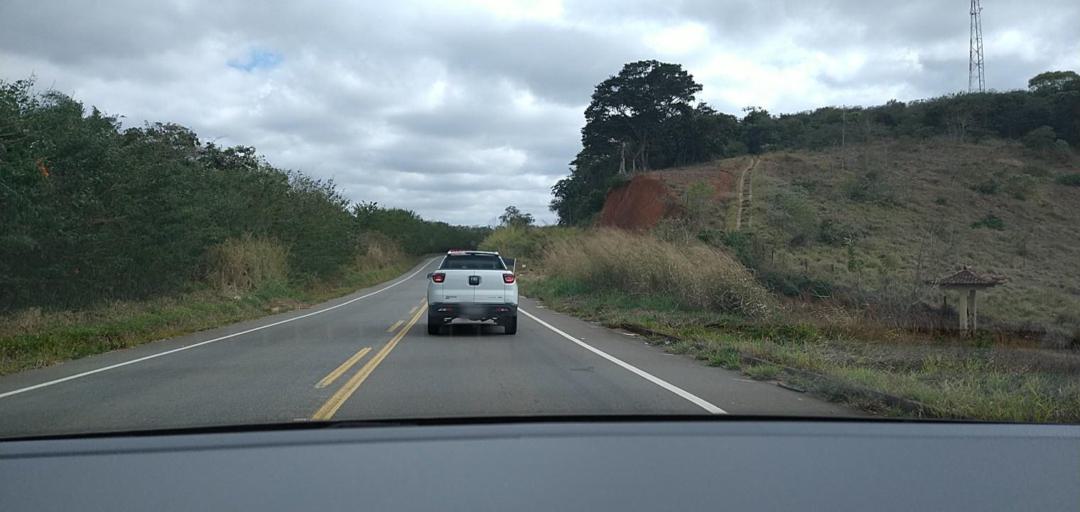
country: BR
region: Minas Gerais
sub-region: Ponte Nova
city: Ponte Nova
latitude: -20.5363
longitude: -42.8907
